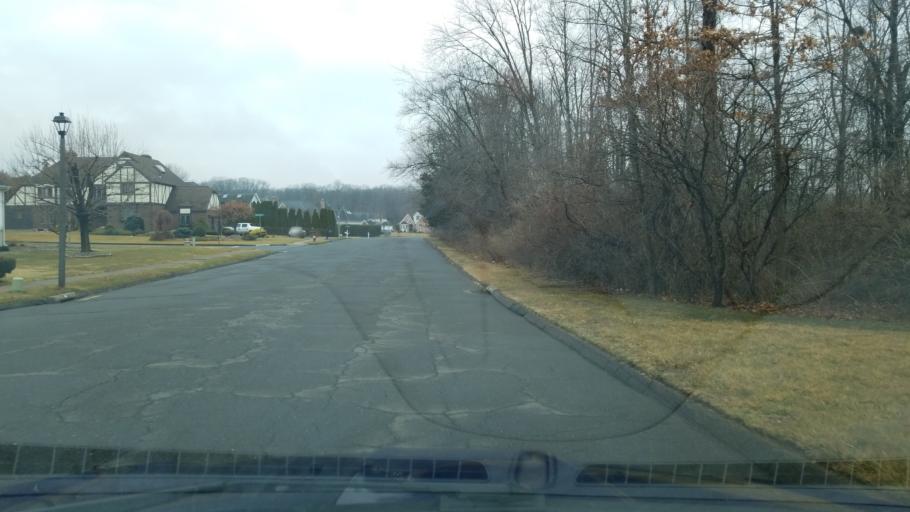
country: US
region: Connecticut
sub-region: Hartford County
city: Newington
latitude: 41.6754
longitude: -72.6968
